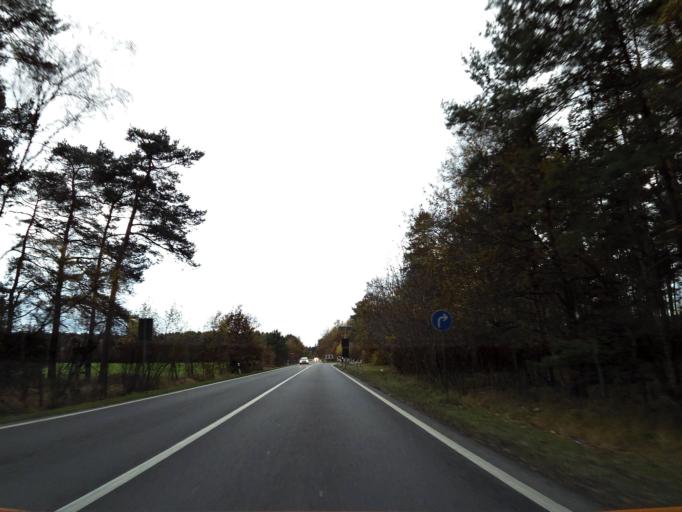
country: DE
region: Lower Saxony
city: Hademstorf
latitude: 52.7733
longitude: 9.6696
